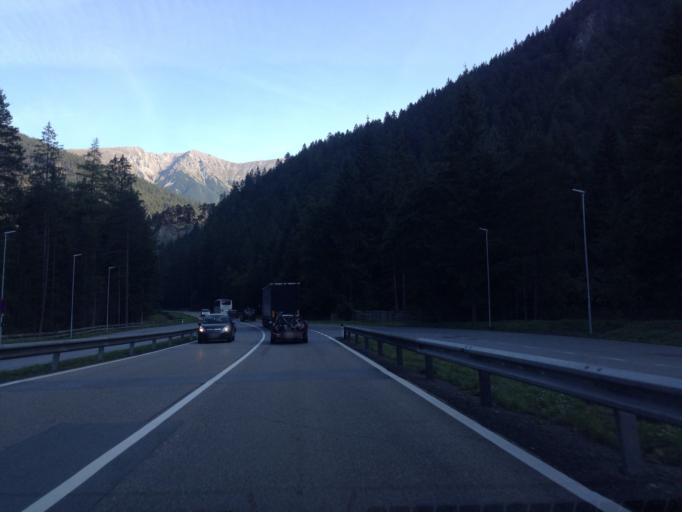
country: AT
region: Tyrol
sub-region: Politischer Bezirk Imst
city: Nassereith
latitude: 47.3346
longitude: 10.8188
